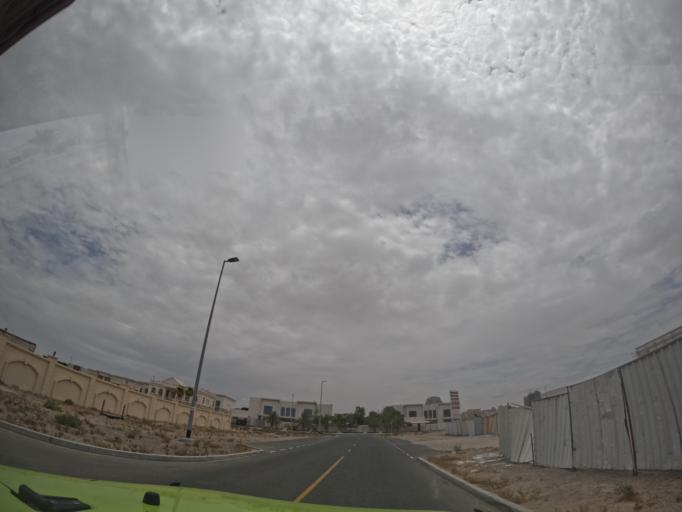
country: AE
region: Dubai
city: Dubai
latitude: 25.1319
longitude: 55.3701
